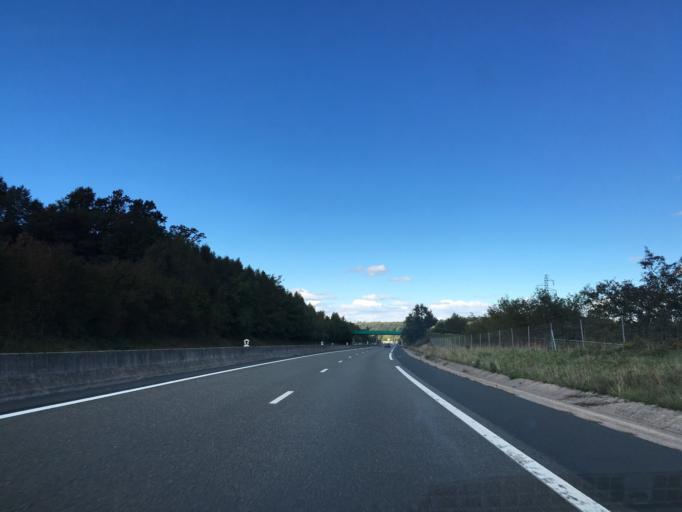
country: FR
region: Lorraine
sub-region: Departement de Meurthe-et-Moselle
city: Baccarat
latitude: 48.4148
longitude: 6.7970
